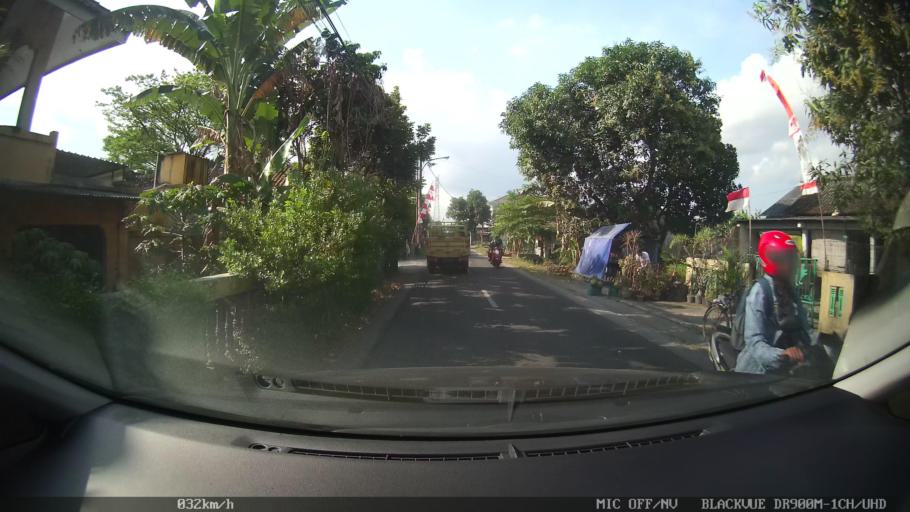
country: ID
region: Daerah Istimewa Yogyakarta
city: Kasihan
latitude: -7.8416
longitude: 110.3439
